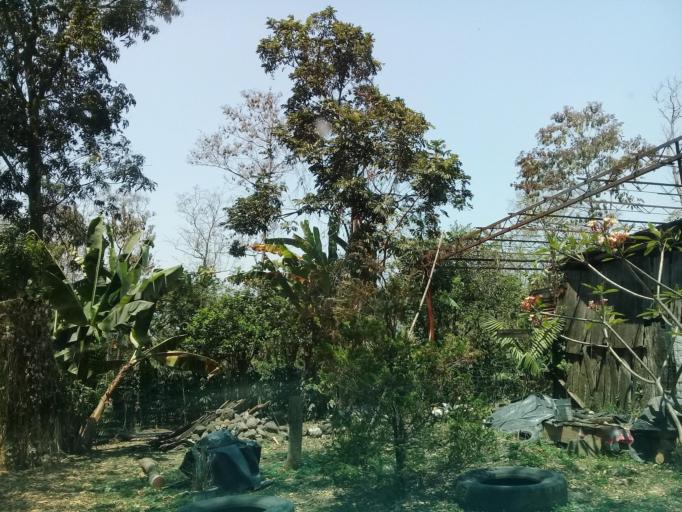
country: MX
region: Veracruz
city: Paraje Nuevo
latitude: 18.8738
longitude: -96.8752
